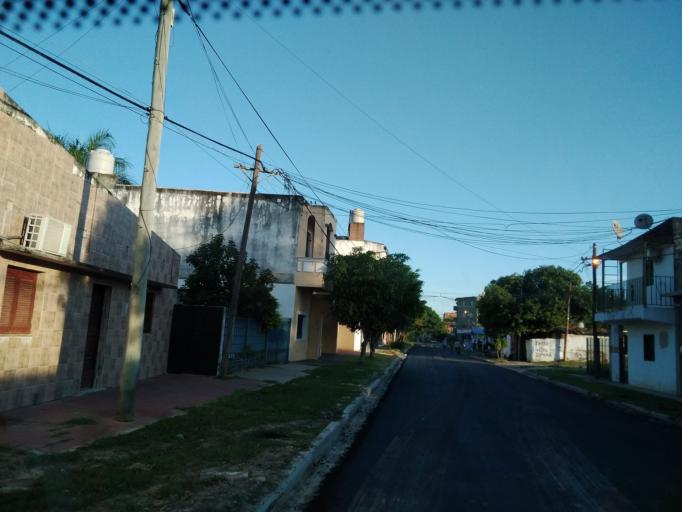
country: AR
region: Corrientes
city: Corrientes
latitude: -27.4622
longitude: -58.7836
